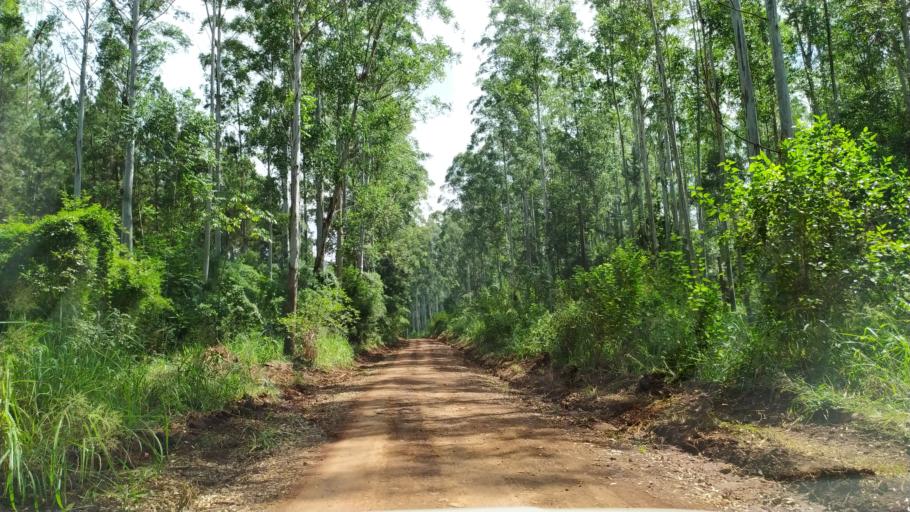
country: AR
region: Misiones
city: Puerto Piray
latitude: -26.5319
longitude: -54.6229
